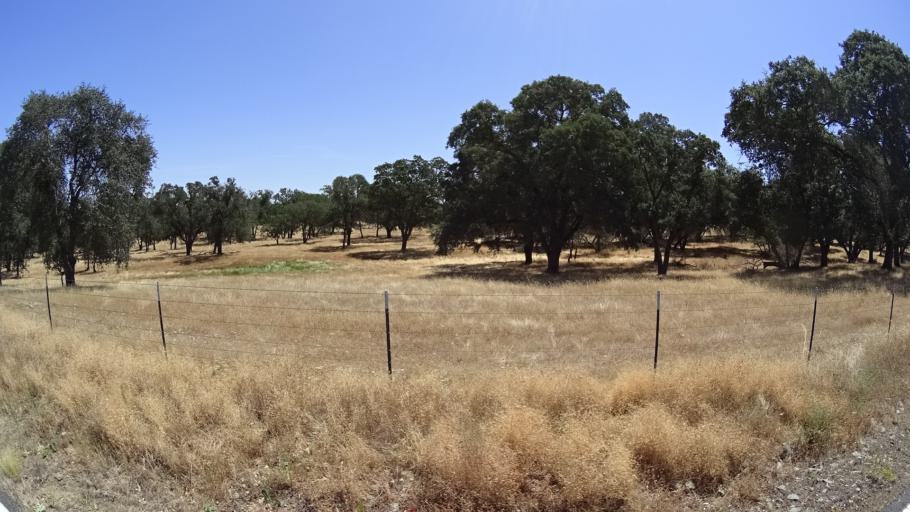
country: US
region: California
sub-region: Calaveras County
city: Rancho Calaveras
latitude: 38.1273
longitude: -120.9449
